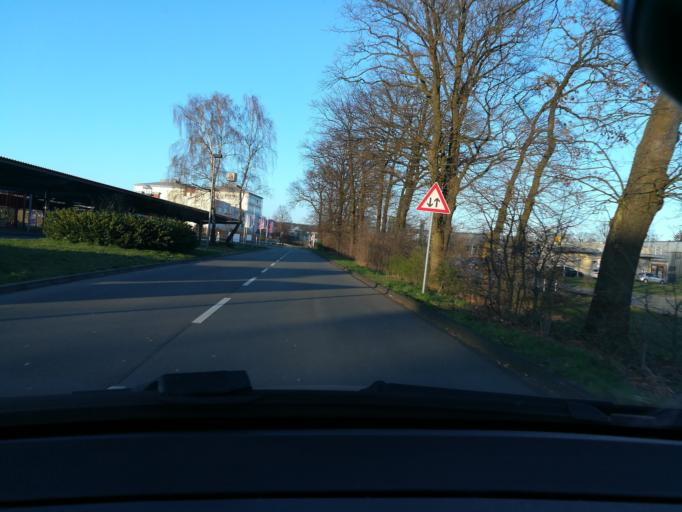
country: DE
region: North Rhine-Westphalia
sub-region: Regierungsbezirk Detmold
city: Verl
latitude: 51.9512
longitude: 8.5718
